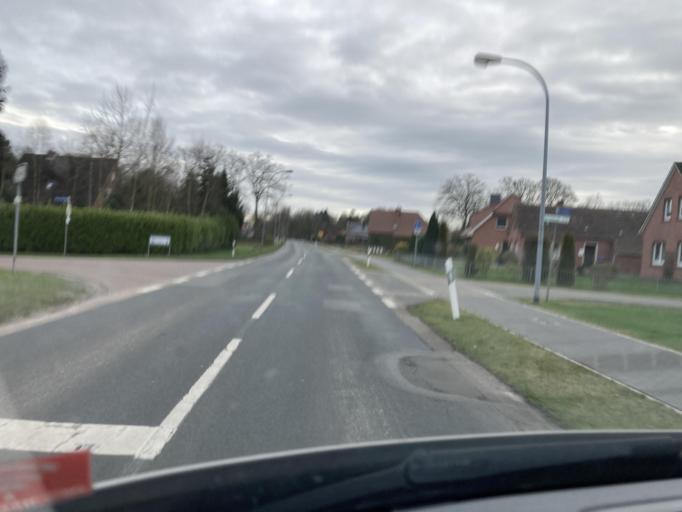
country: DE
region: Lower Saxony
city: Leer
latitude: 53.1474
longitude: 7.4727
